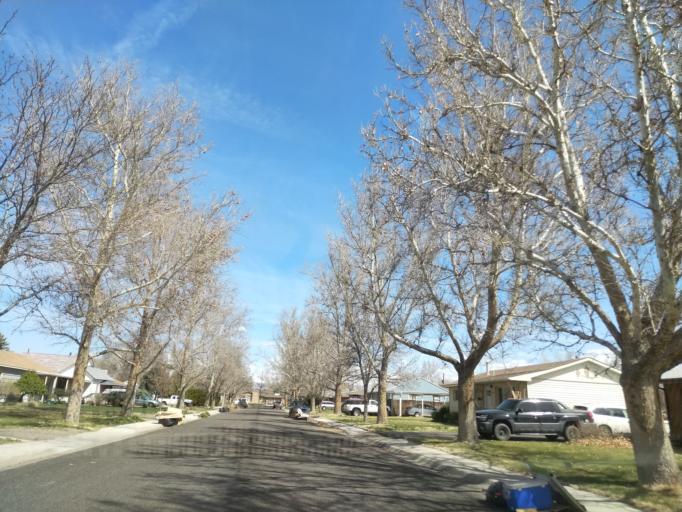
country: US
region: Colorado
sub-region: Mesa County
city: Grand Junction
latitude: 39.0820
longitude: -108.5454
